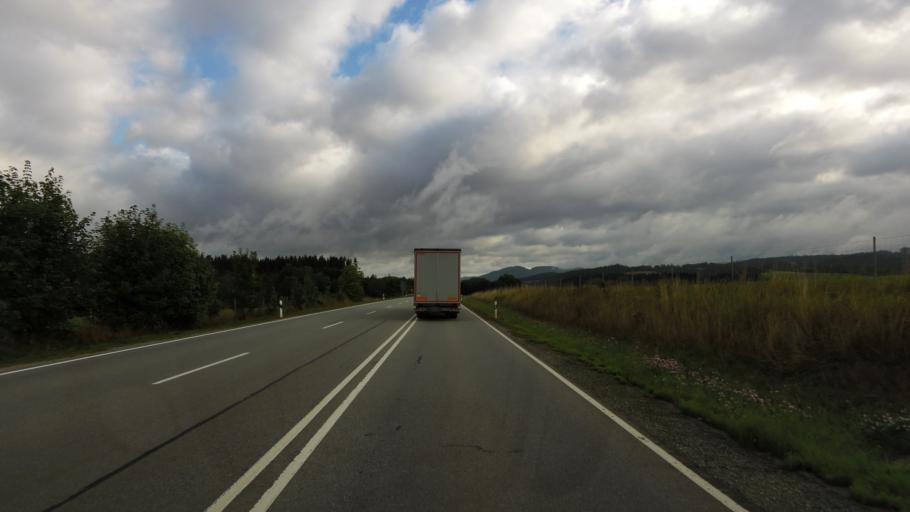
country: DE
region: Bavaria
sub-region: Lower Bavaria
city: Ascha
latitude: 48.9760
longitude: 12.6281
